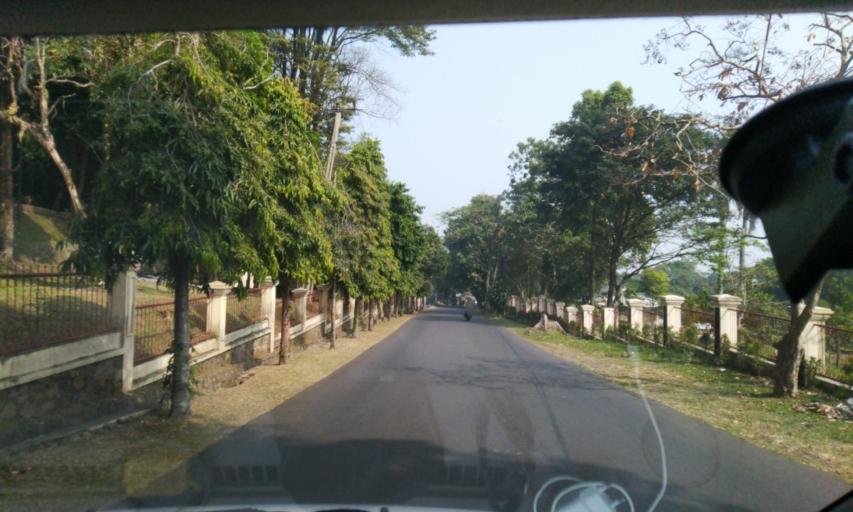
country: ID
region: West Java
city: Caringin
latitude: -6.6619
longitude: 106.8604
